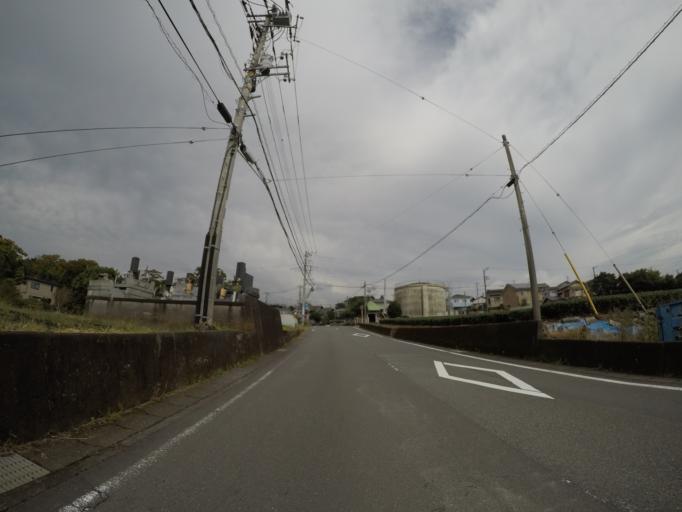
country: JP
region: Shizuoka
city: Fuji
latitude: 35.2182
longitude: 138.6837
